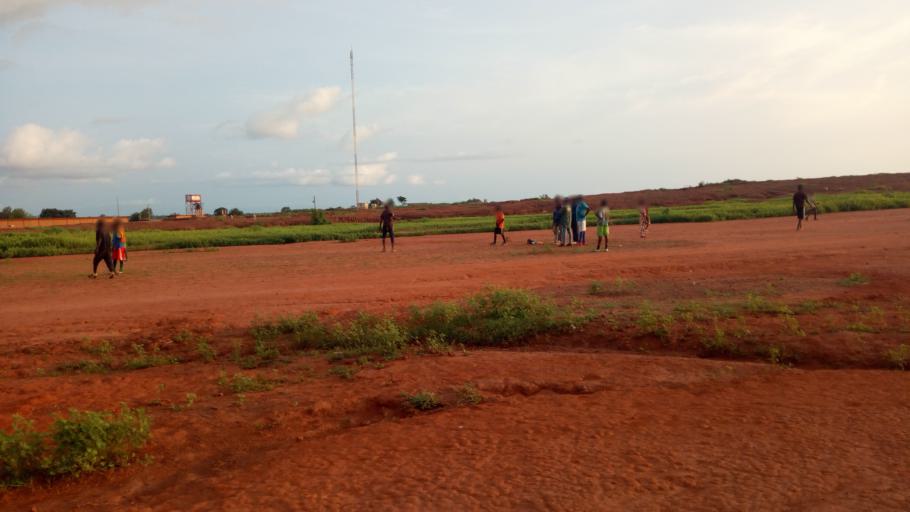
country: ML
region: Sikasso
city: Koutiala
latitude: 12.3745
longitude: -5.4779
